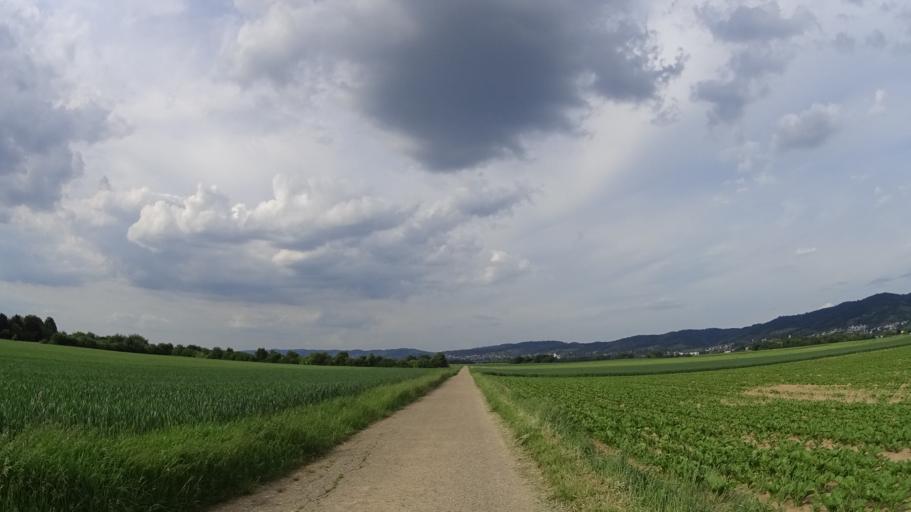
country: DE
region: Baden-Wuerttemberg
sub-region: Karlsruhe Region
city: Ladenburg
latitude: 49.4876
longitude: 8.6283
